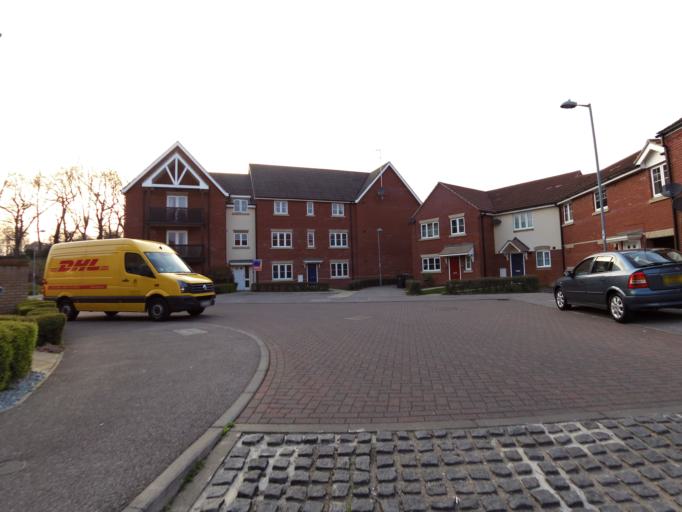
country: GB
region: England
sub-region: Suffolk
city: Ipswich
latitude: 52.0460
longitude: 1.1522
